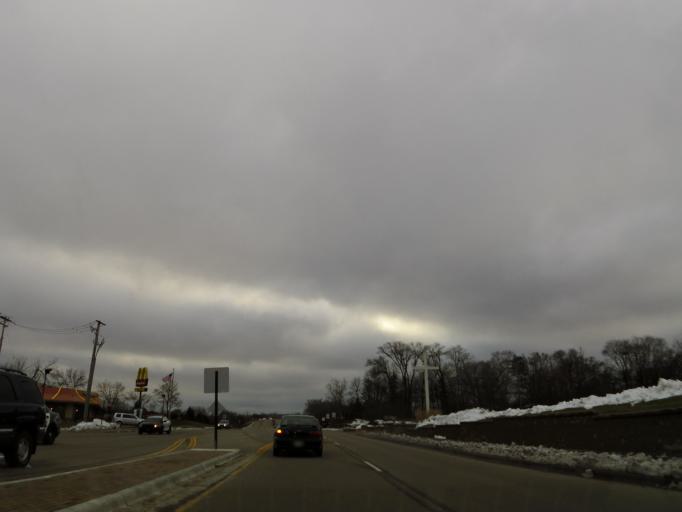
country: US
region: Minnesota
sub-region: Hennepin County
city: Minnetonka Mills
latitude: 44.9205
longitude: -93.4272
